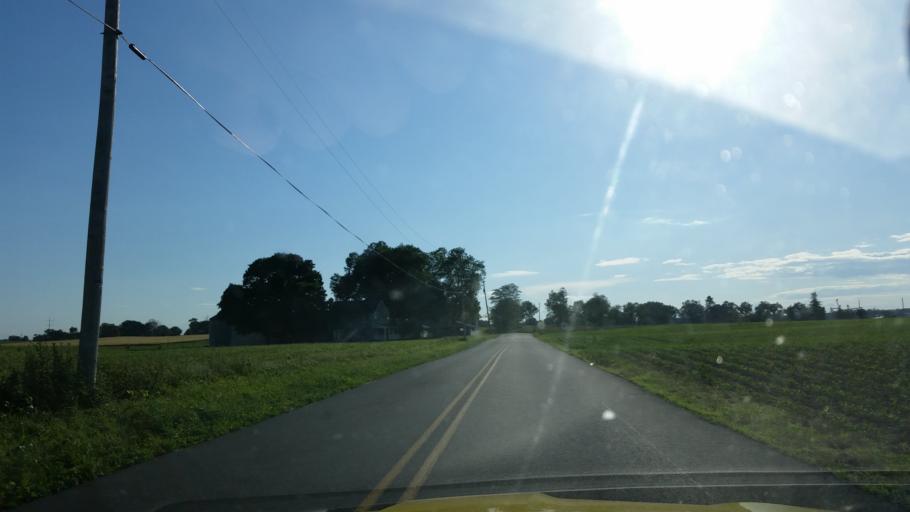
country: US
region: Pennsylvania
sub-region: Lebanon County
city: Avon
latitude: 40.3432
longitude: -76.3663
